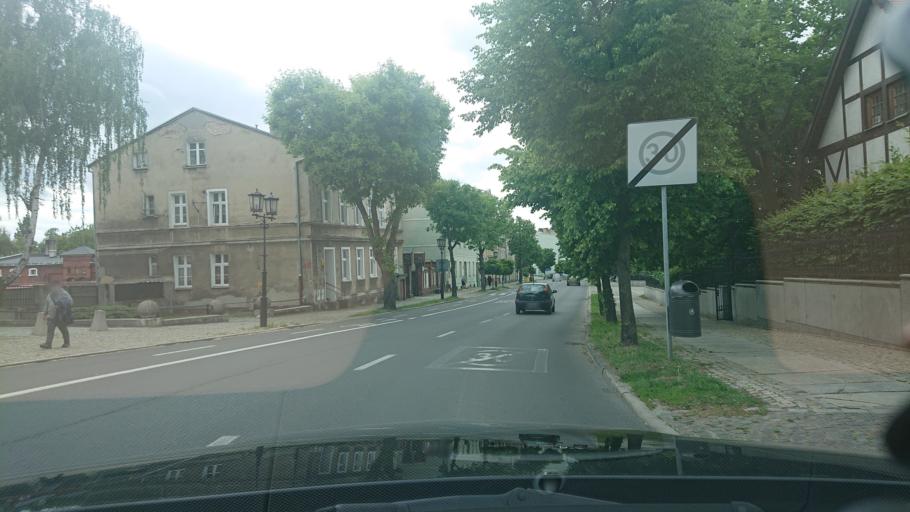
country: PL
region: Greater Poland Voivodeship
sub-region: Powiat gnieznienski
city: Gniezno
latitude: 52.5364
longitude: 17.5908
